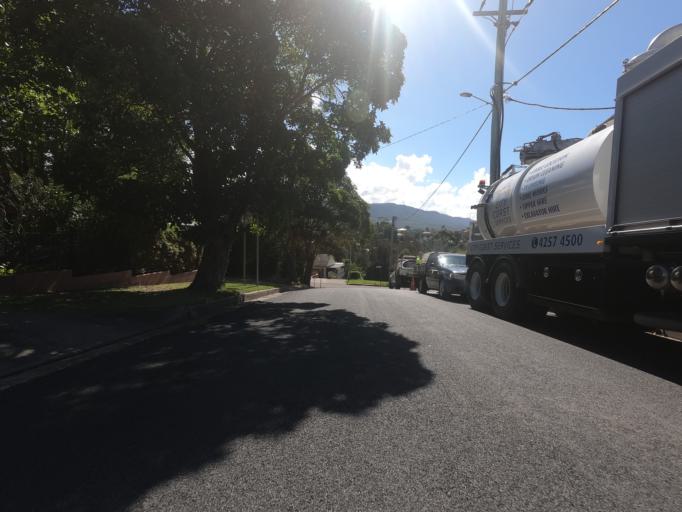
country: AU
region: New South Wales
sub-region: Wollongong
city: Bulli
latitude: -34.3334
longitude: 150.9181
